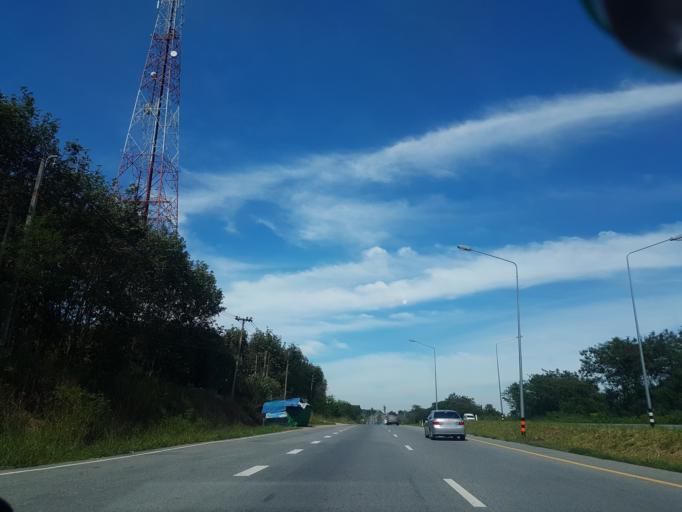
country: TH
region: Rayong
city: Ban Chang
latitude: 12.8718
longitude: 101.0236
